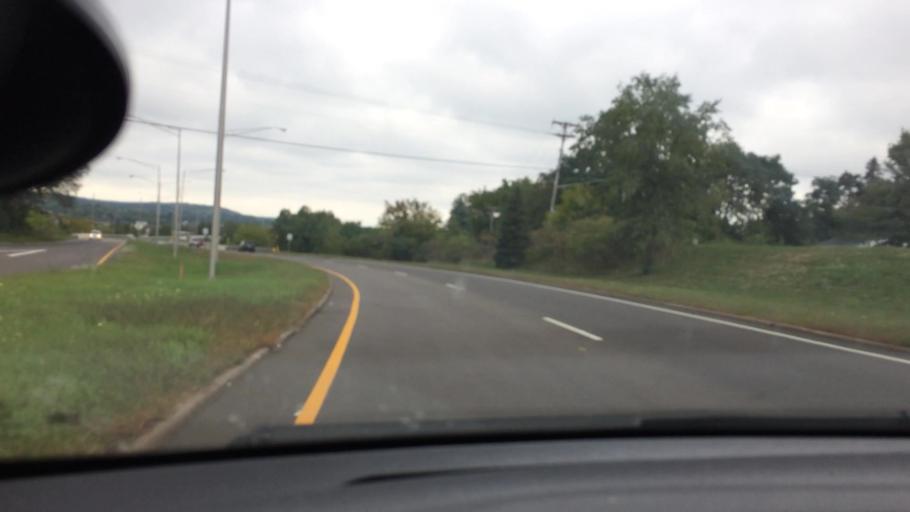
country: US
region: Wisconsin
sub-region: Chippewa County
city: Chippewa Falls
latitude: 44.9263
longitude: -91.3832
